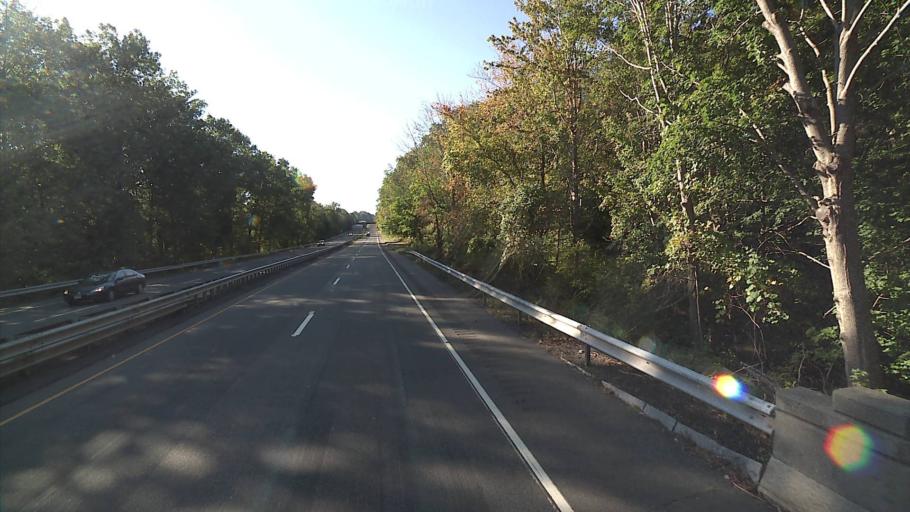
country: US
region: Connecticut
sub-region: New Haven County
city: Meriden
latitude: 41.5464
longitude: -72.7726
